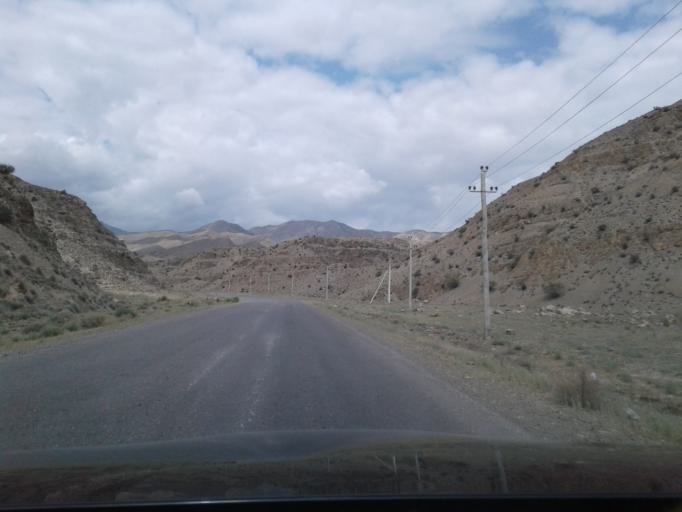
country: TM
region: Ahal
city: Baharly
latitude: 38.5026
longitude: 57.0944
